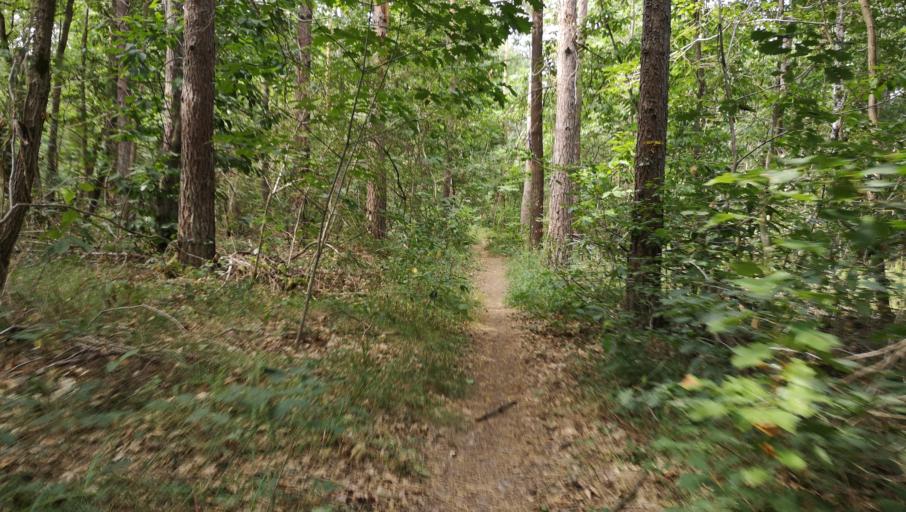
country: FR
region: Centre
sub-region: Departement du Loiret
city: Chanteau
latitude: 47.9428
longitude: 1.9800
